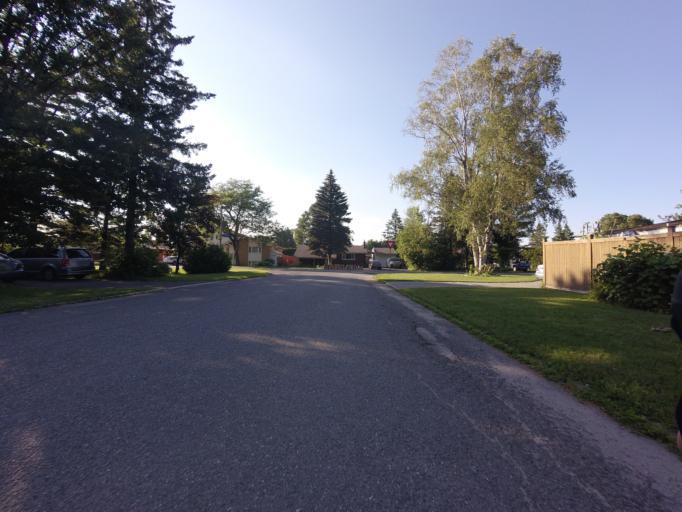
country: CA
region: Ontario
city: Bells Corners
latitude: 45.3272
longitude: -75.7603
